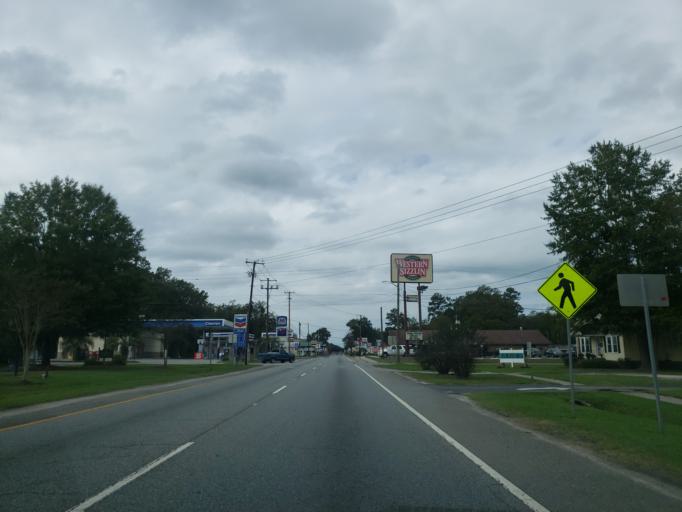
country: US
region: Georgia
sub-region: Chatham County
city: Pooler
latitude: 32.1143
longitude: -81.2432
